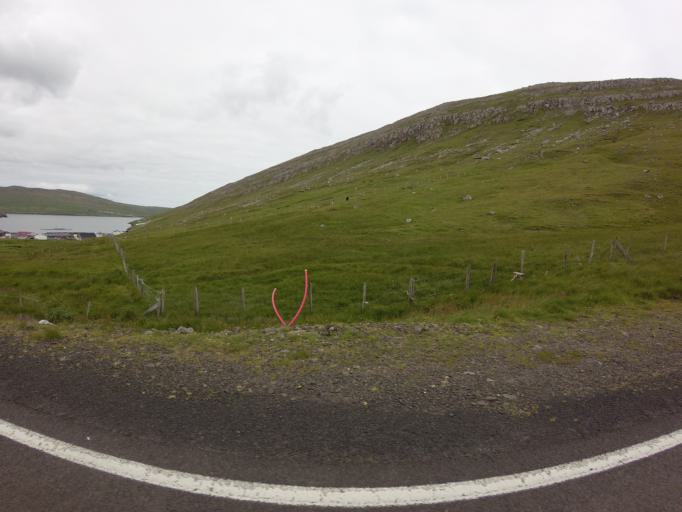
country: FO
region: Suduroy
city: Vagur
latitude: 61.4386
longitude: -6.7701
